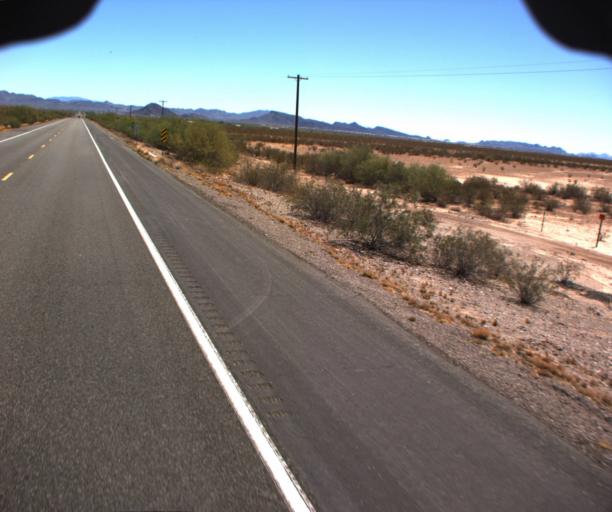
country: US
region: Arizona
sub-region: La Paz County
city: Salome
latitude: 33.7053
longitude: -113.8330
